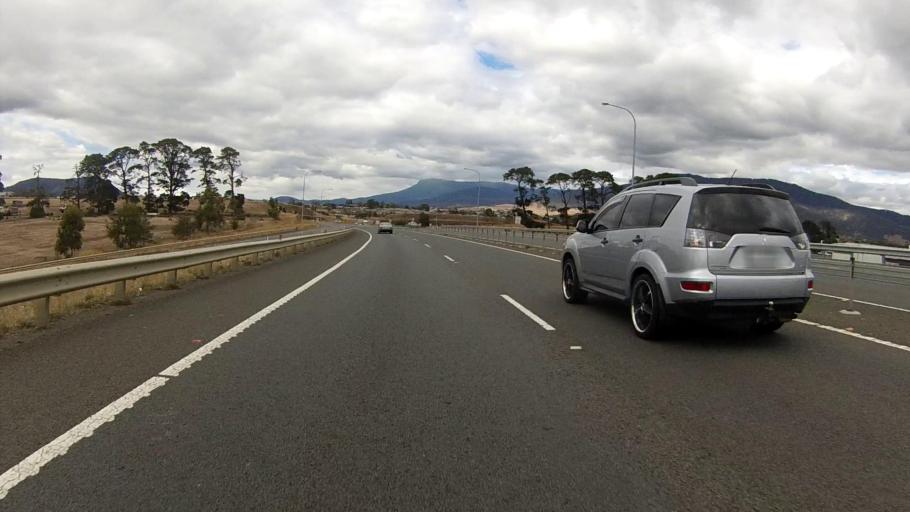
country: AU
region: Tasmania
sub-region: Brighton
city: Bridgewater
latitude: -42.7265
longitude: 147.2373
